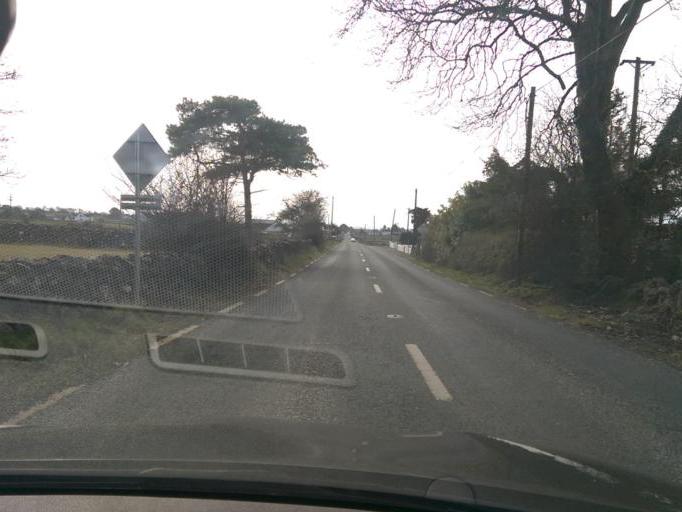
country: IE
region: Connaught
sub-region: County Galway
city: Tuam
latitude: 53.4001
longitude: -8.8316
